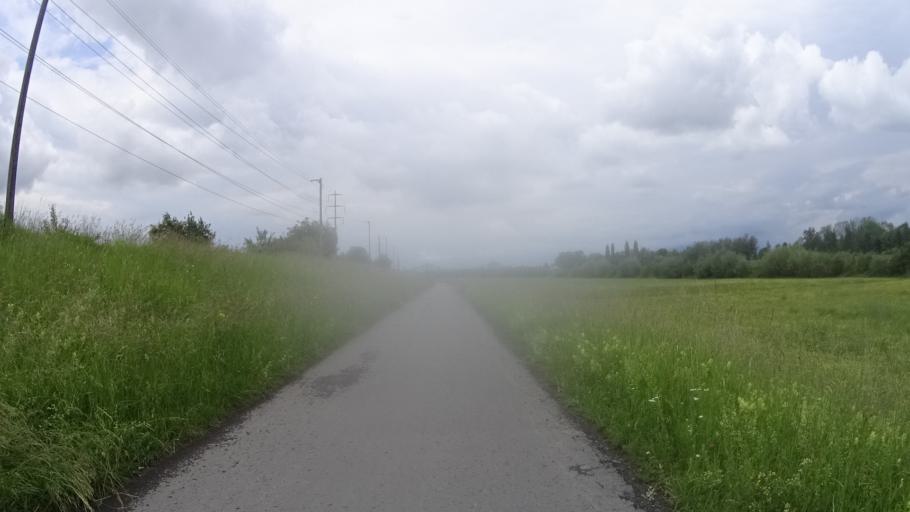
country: CH
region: Saint Gallen
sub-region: Wahlkreis Rheintal
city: Diepoldsau
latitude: 47.4022
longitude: 9.6492
